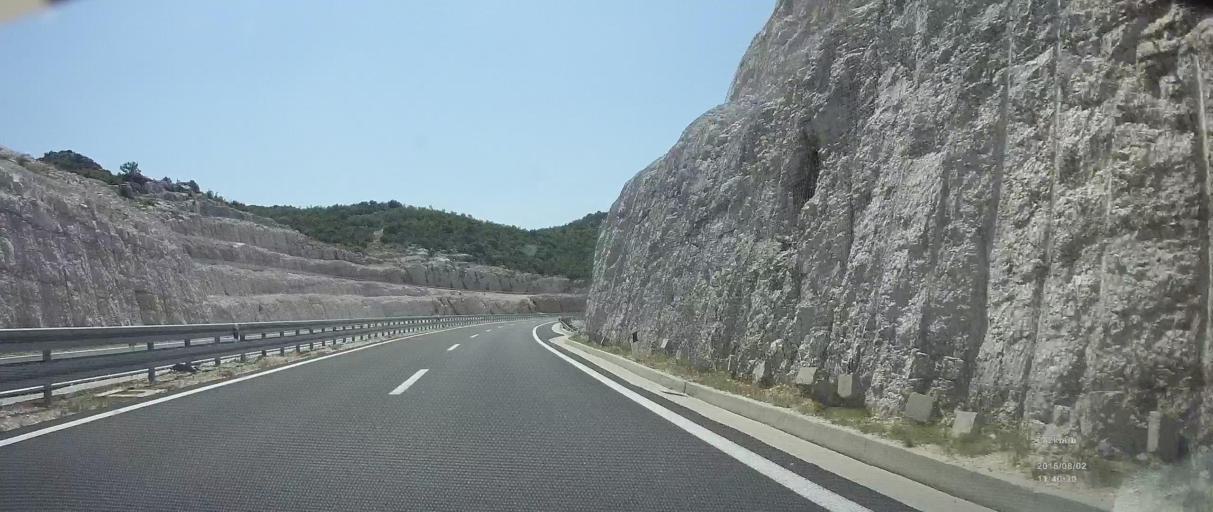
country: HR
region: Dubrovacko-Neretvanska
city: Komin
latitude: 43.0739
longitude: 17.4920
